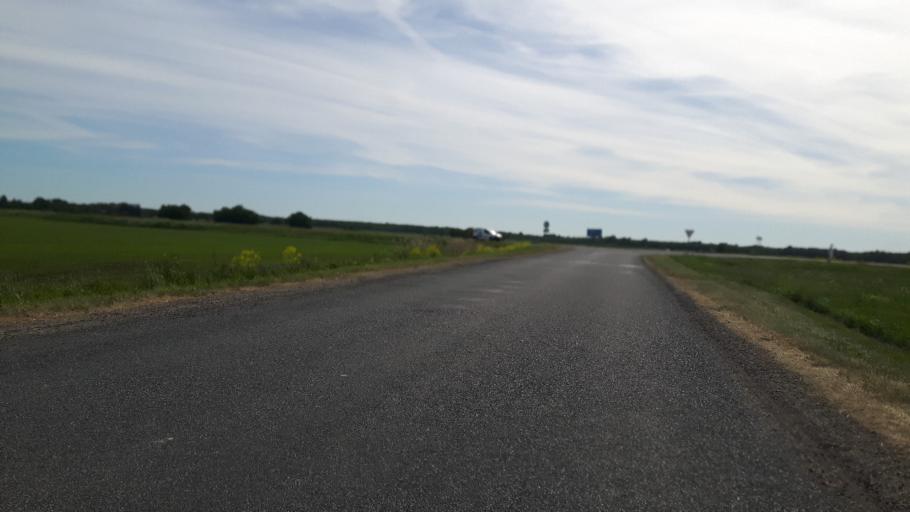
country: EE
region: Harju
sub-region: Raasiku vald
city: Arukula
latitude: 59.4213
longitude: 25.0788
